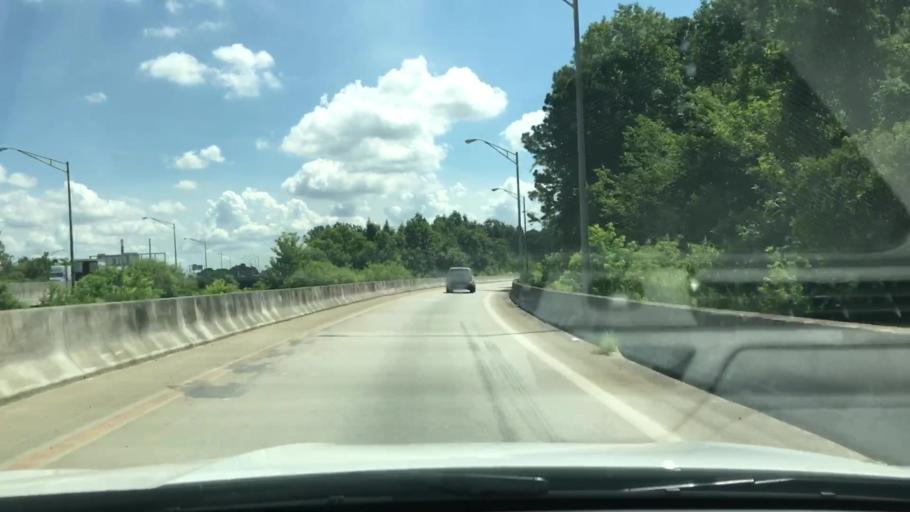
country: US
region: South Carolina
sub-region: Berkeley County
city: Hanahan
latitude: 32.8940
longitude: -79.9910
